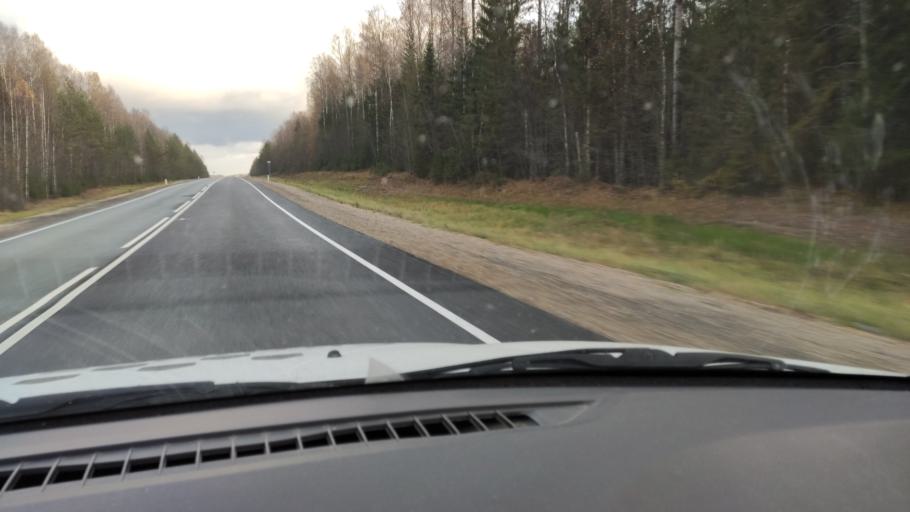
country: RU
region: Kirov
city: Chernaya Kholunitsa
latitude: 58.7994
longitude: 51.8650
